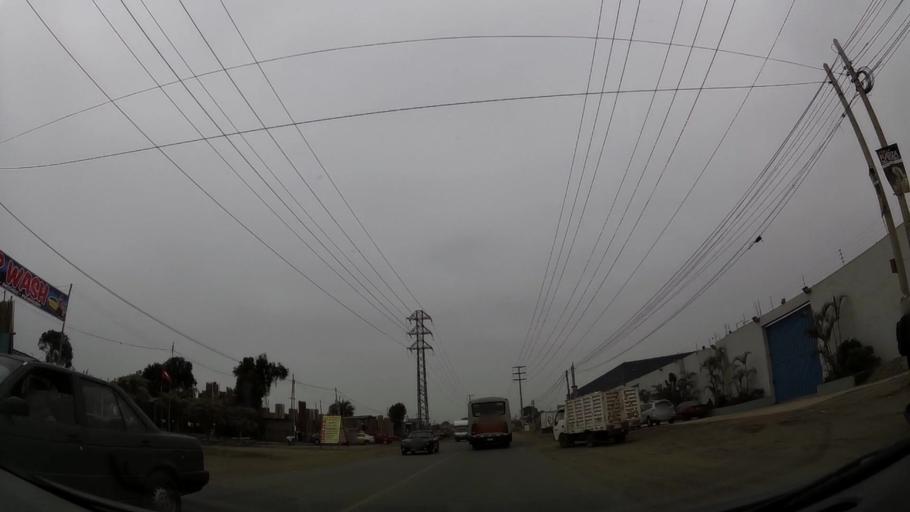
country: PE
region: Lima
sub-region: Lima
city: Punta Hermosa
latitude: -12.2683
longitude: -76.8774
